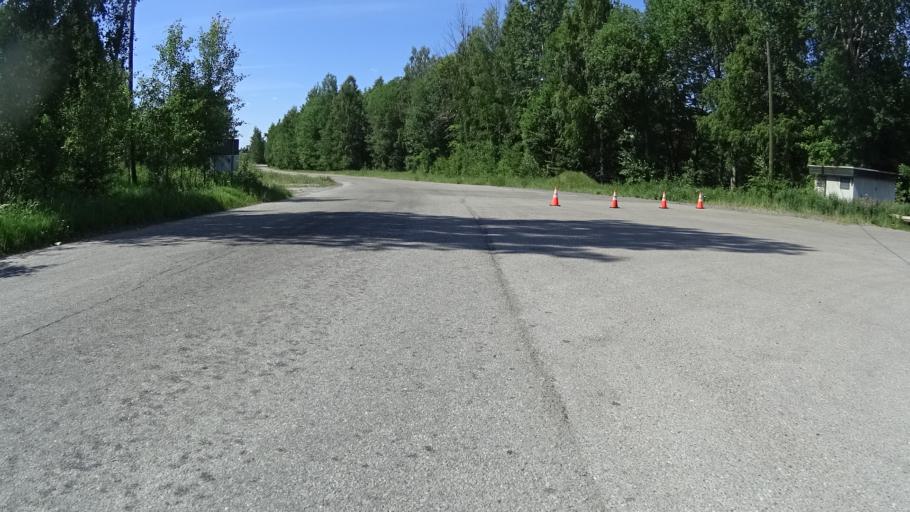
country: FI
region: Uusimaa
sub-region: Raaseporin
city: Pohja
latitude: 60.0931
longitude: 23.5714
